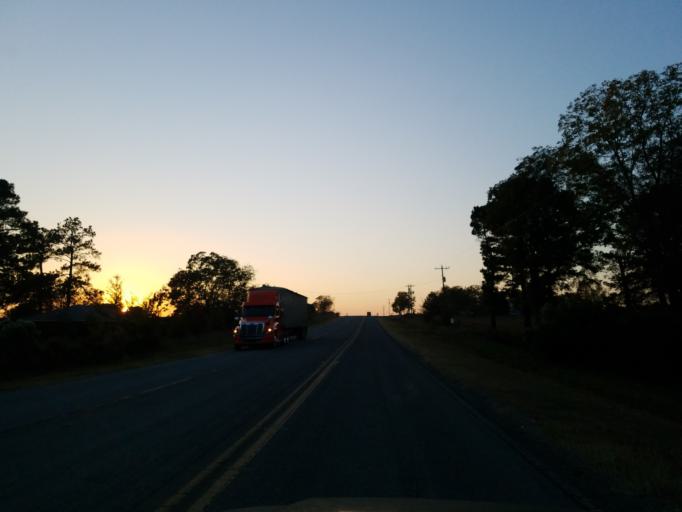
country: US
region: Georgia
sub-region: Ben Hill County
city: Fitzgerald
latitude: 31.7202
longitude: -83.4054
